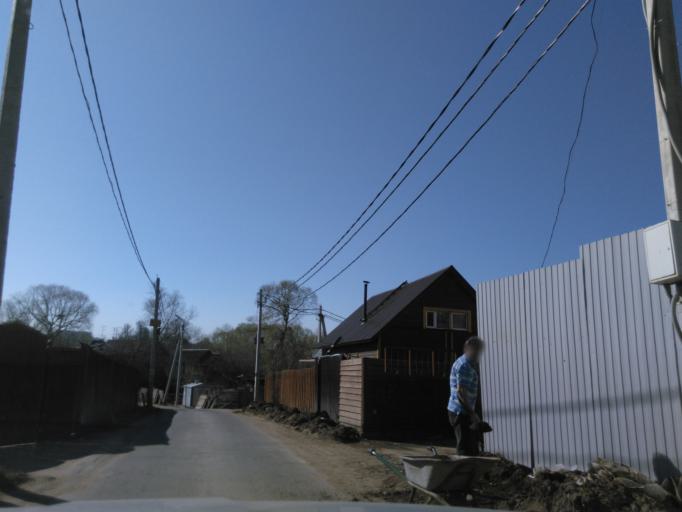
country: RU
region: Moscow
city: Khimki
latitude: 55.8775
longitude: 37.3757
